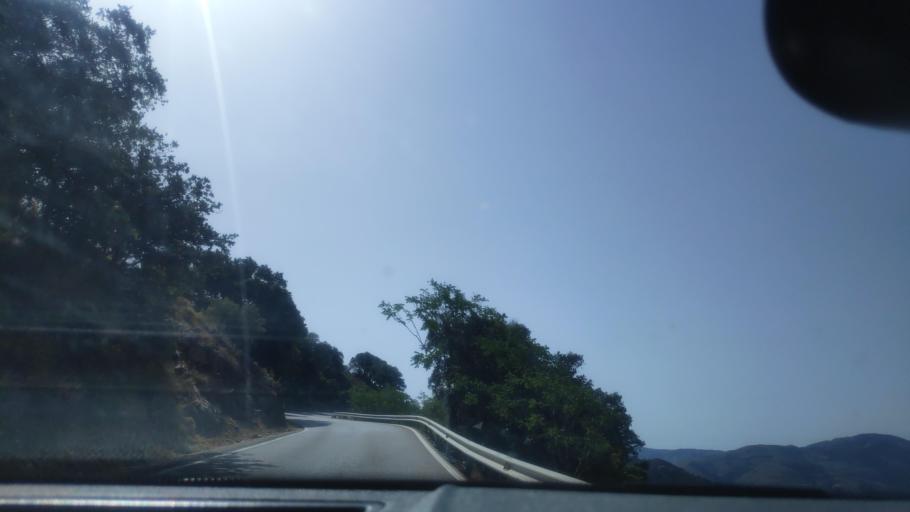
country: ES
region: Andalusia
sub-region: Provincia de Granada
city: Pampaneira
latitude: 36.9246
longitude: -3.3533
